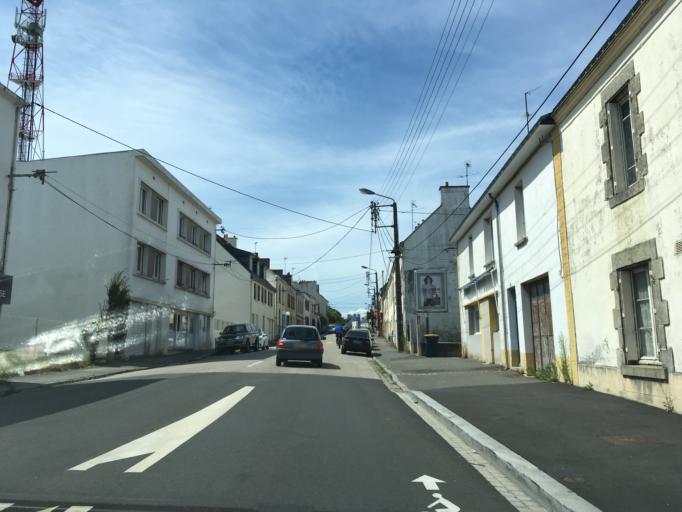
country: FR
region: Brittany
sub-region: Departement du Morbihan
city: Lorient
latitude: 47.7432
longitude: -3.3893
